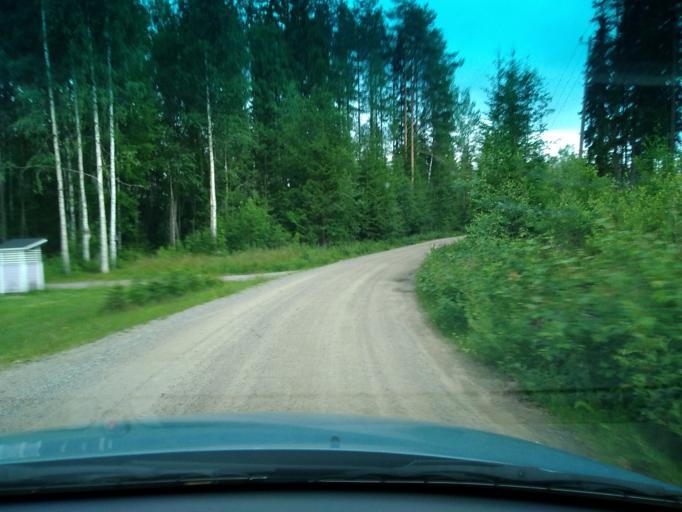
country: FI
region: Central Finland
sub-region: Saarijaervi-Viitasaari
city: Pylkoenmaeki
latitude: 62.7614
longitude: 24.9790
